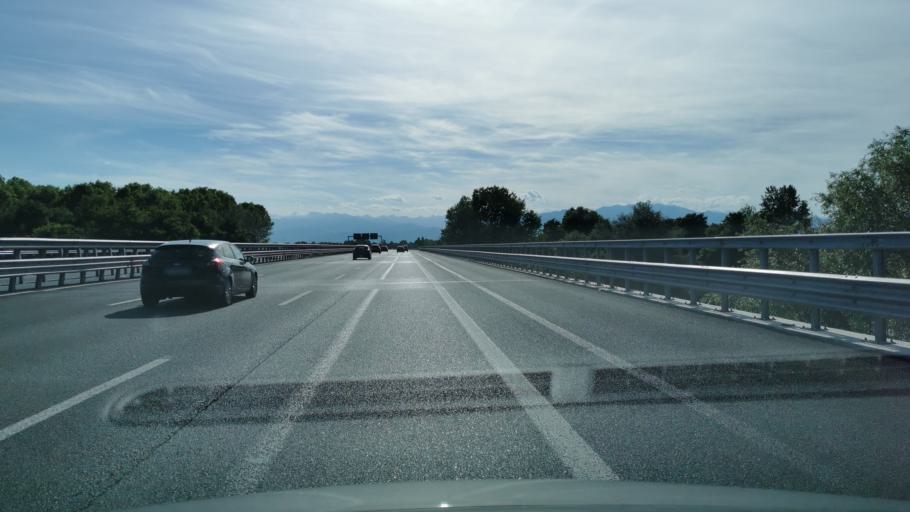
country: IT
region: Piedmont
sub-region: Provincia di Torino
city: La Loggia
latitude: 44.9713
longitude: 7.6941
